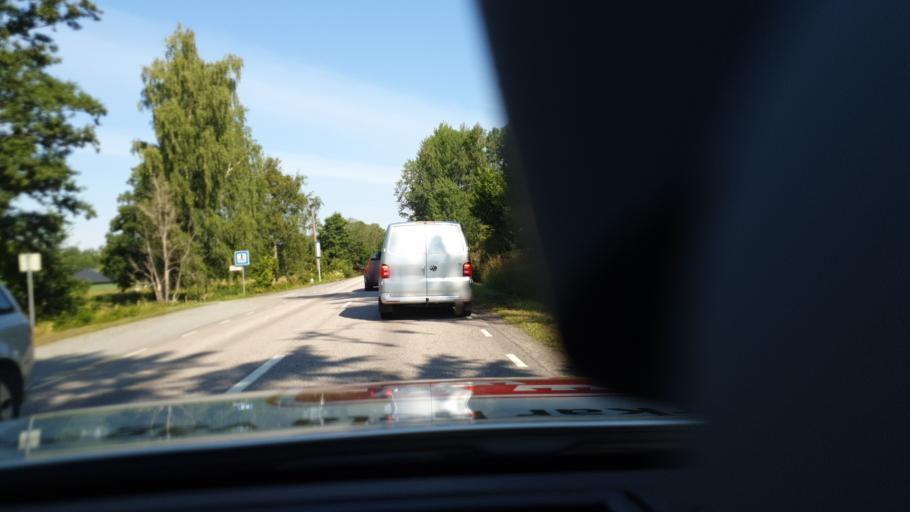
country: SE
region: Stockholm
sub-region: Norrtalje Kommun
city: Arno
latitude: 59.9921
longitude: 18.8074
